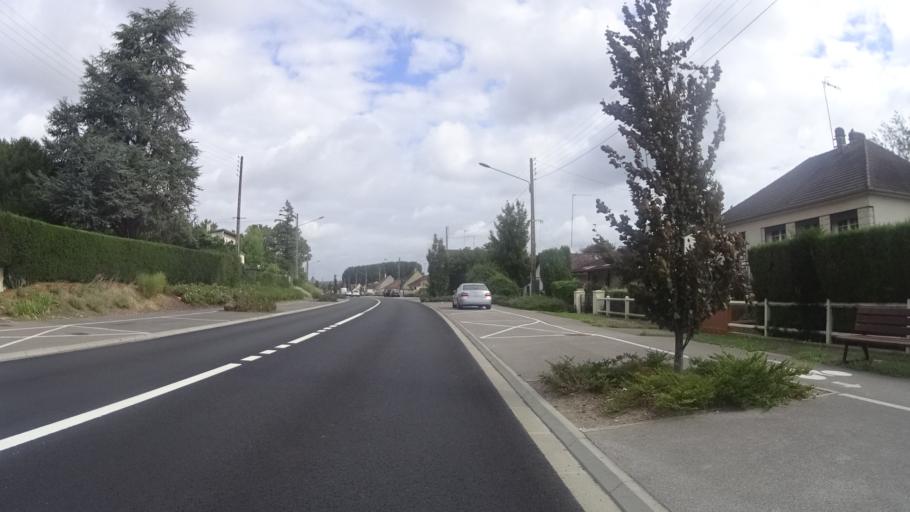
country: FR
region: Picardie
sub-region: Departement de l'Oise
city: Choisy-au-Bac
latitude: 49.4445
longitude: 2.8635
